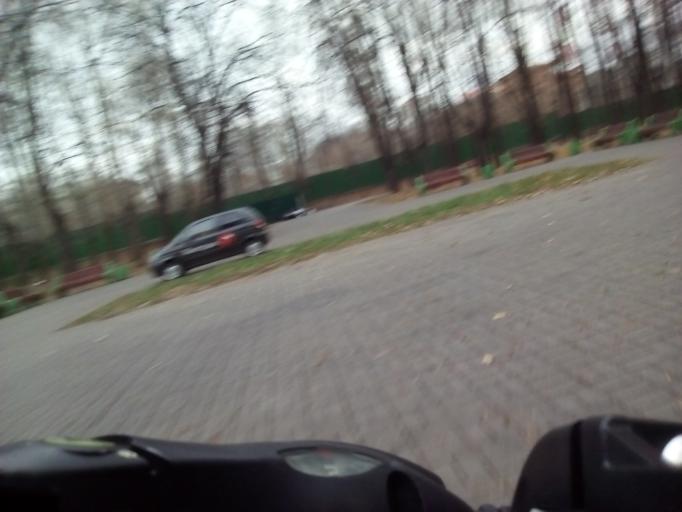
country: RU
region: Moscow
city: Lefortovo
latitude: 55.7532
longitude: 37.7170
